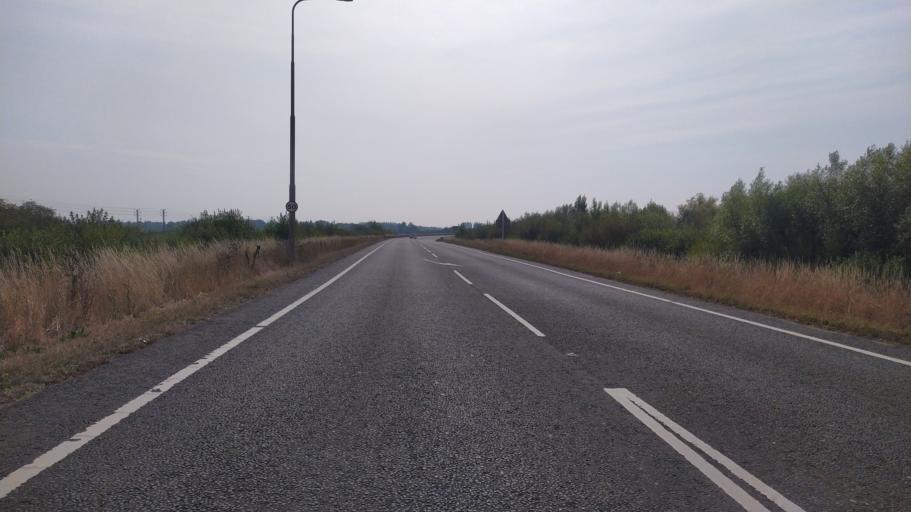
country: GB
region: England
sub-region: West Sussex
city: Bognor Regis
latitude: 50.8065
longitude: -0.6828
